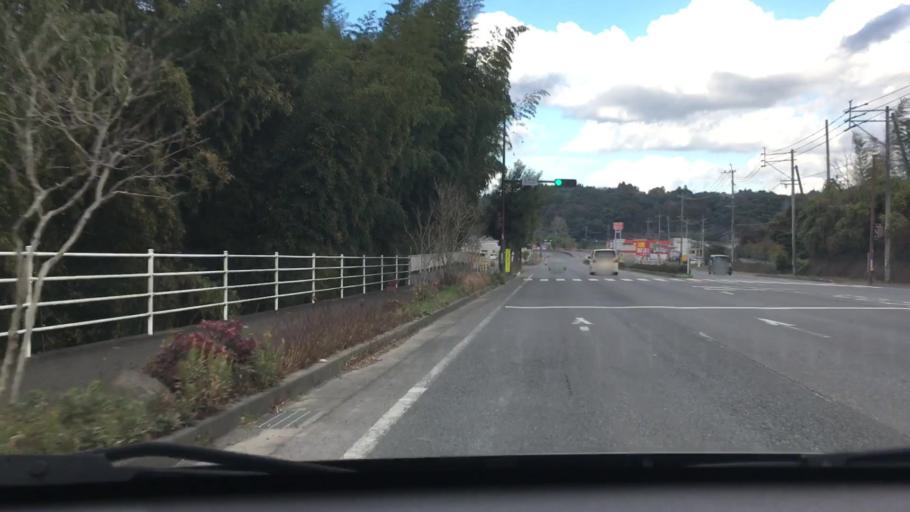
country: JP
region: Oita
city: Oita
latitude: 33.1294
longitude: 131.6578
